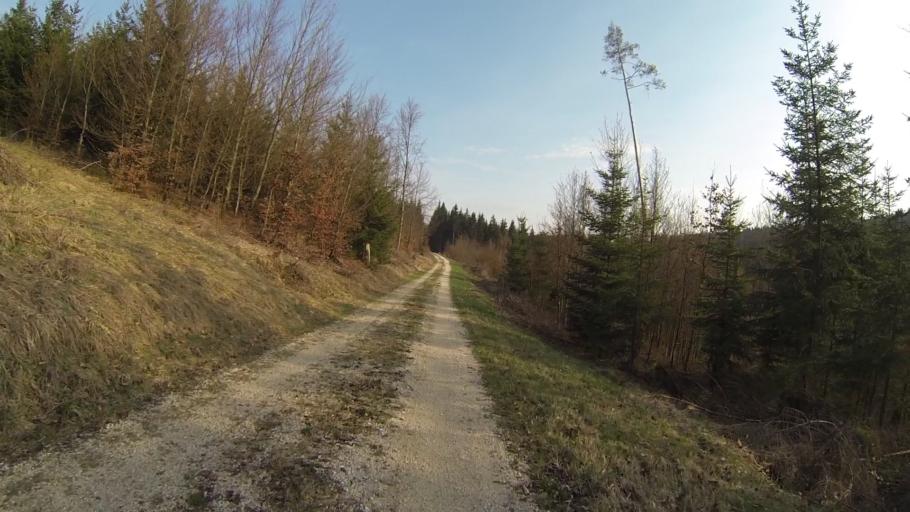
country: DE
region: Baden-Wuerttemberg
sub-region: Regierungsbezirk Stuttgart
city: Heidenheim an der Brenz
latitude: 48.6562
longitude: 10.1112
